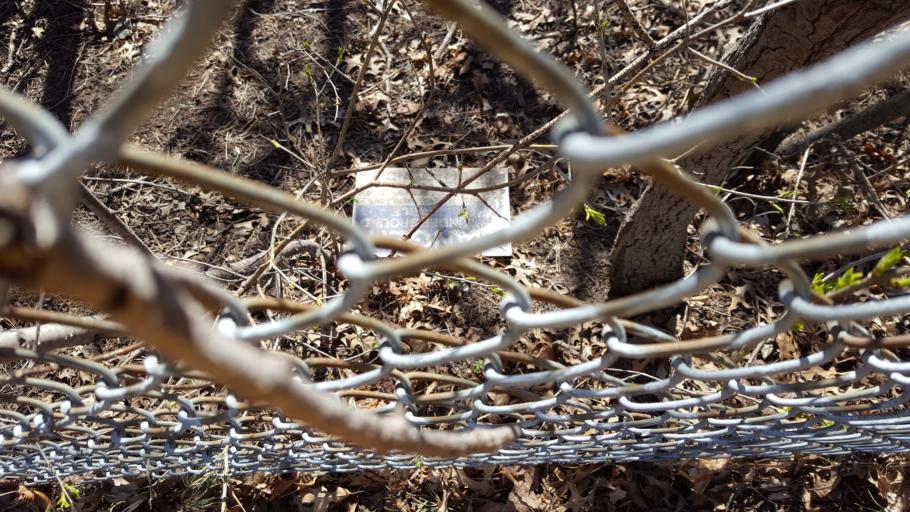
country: US
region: Illinois
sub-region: Lake County
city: Deerfield
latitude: 42.1538
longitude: -87.8420
